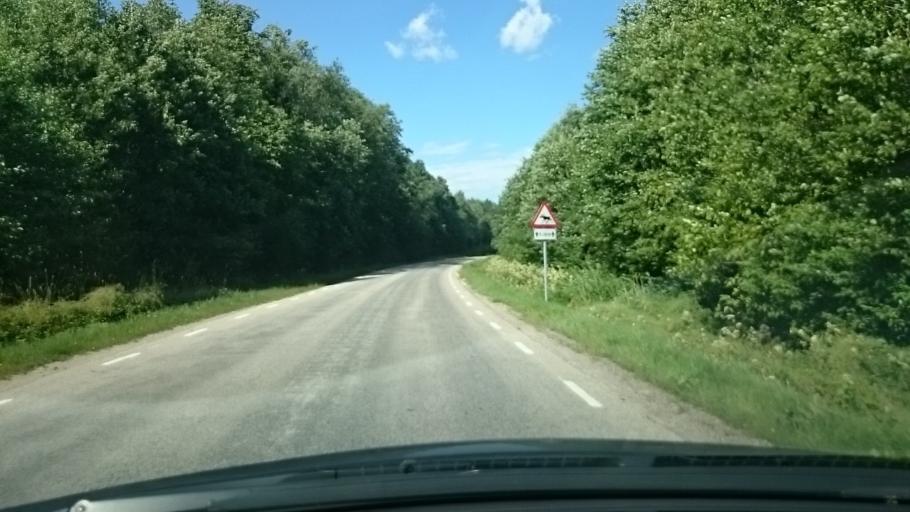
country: EE
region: Laeaene
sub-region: Haapsalu linn
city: Haapsalu
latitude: 59.0434
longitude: 23.5081
